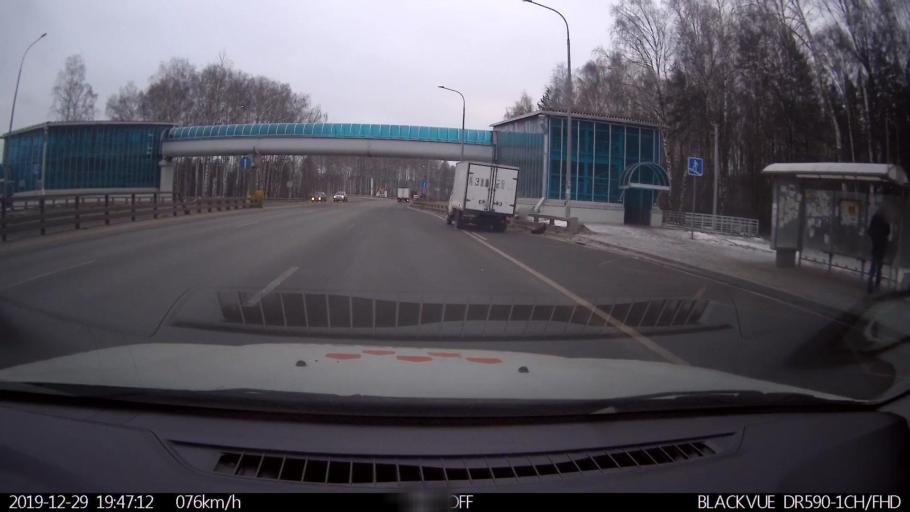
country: RU
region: Nizjnij Novgorod
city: Neklyudovo
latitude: 56.3952
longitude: 44.0050
